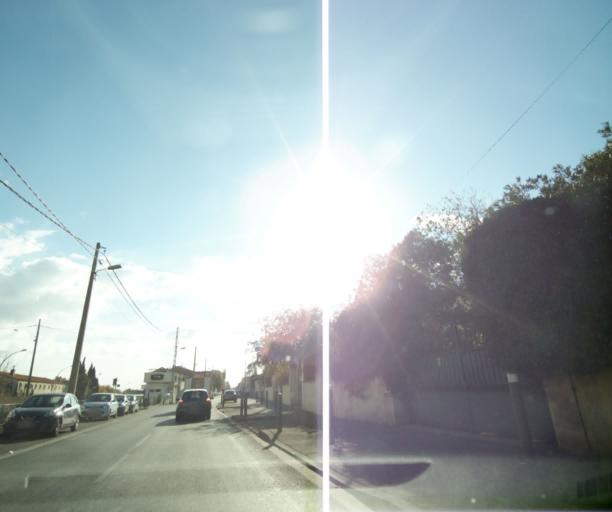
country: FR
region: Provence-Alpes-Cote d'Azur
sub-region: Departement des Bouches-du-Rhone
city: Marseille 15
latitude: 43.3838
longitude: 5.3585
